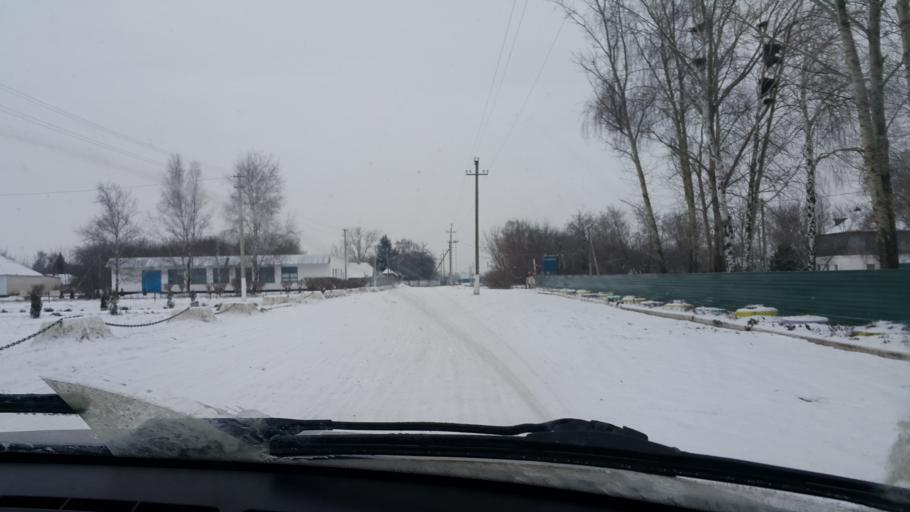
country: RU
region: Tambov
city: Inzhavino
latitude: 52.4686
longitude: 42.3821
